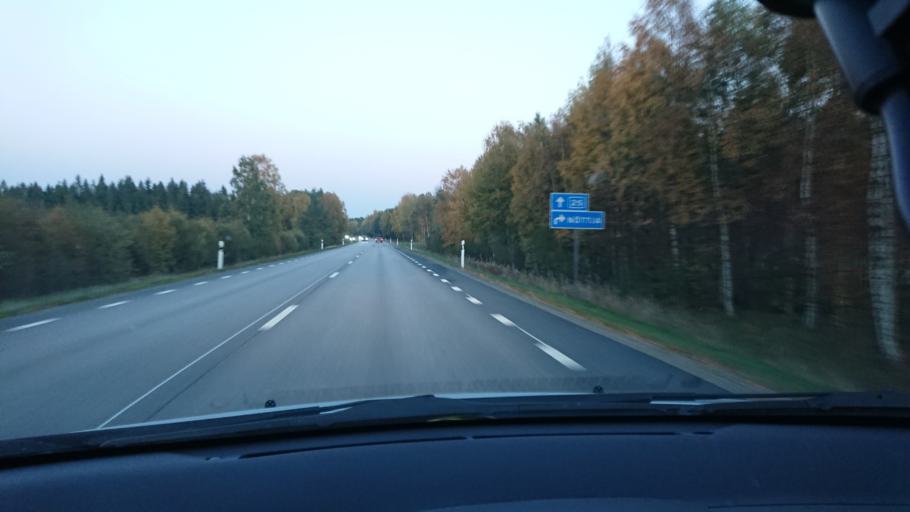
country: SE
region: Kronoberg
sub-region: Markaryds Kommun
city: Stromsnasbruk
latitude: 56.7558
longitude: 13.7443
